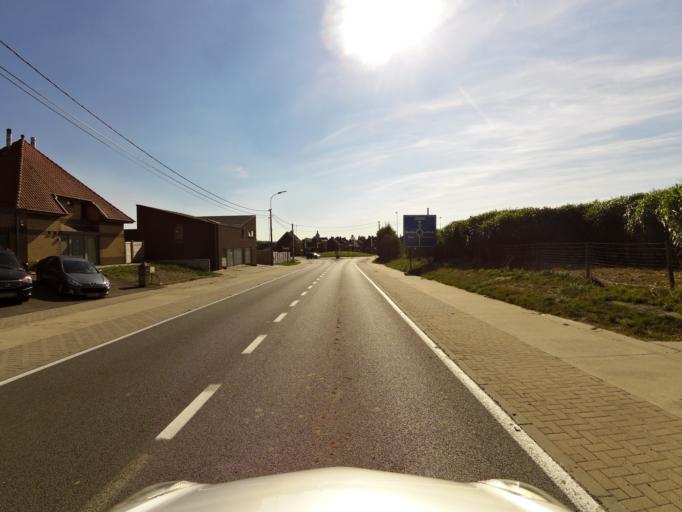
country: BE
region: Flanders
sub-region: Provincie West-Vlaanderen
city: Poperinge
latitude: 50.8644
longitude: 2.7339
